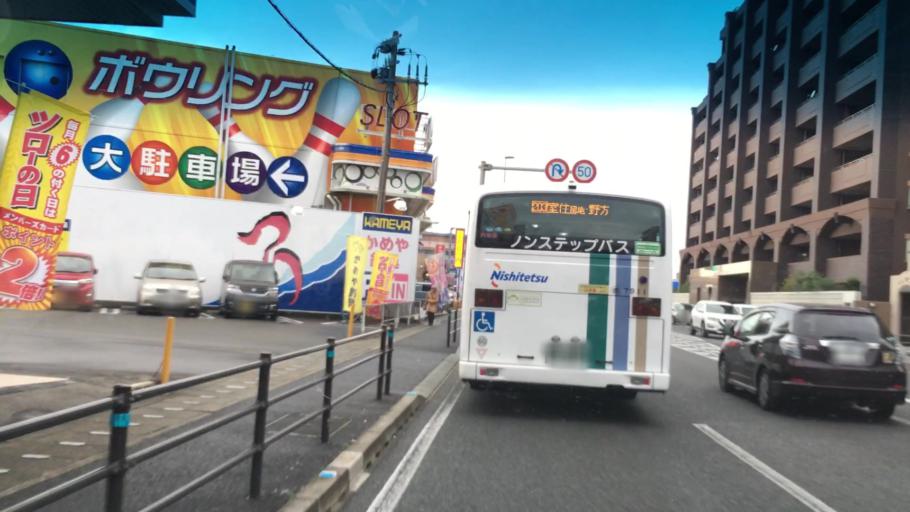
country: JP
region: Fukuoka
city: Fukuoka-shi
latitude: 33.5673
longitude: 130.3396
